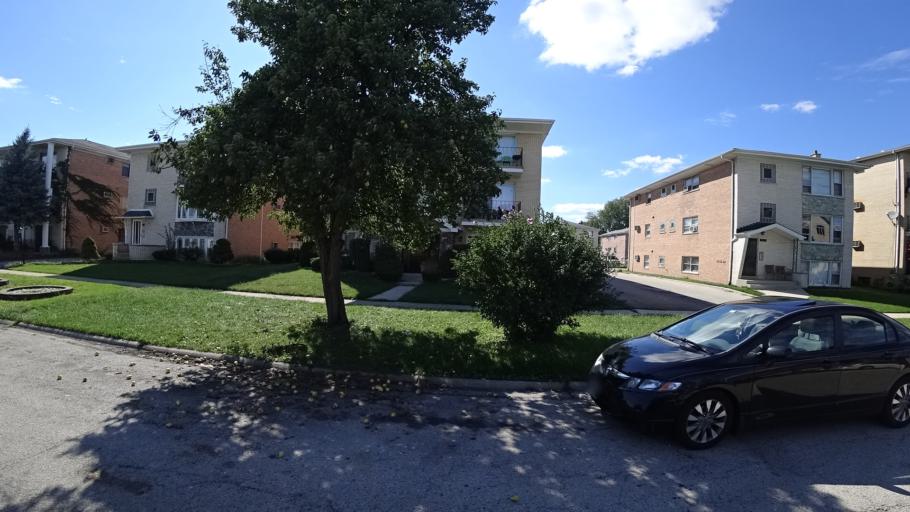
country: US
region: Illinois
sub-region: Cook County
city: Chicago Ridge
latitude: 41.7033
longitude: -87.7695
